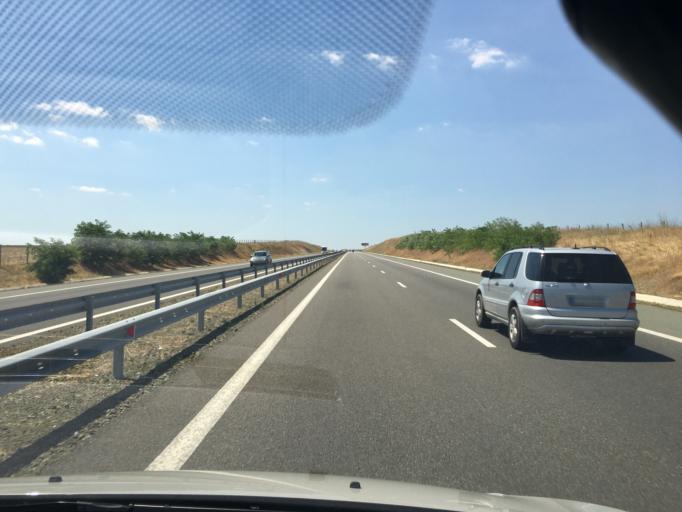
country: BG
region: Burgas
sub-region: Obshtina Karnobat
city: Karnobat
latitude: 42.5888
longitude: 26.9626
